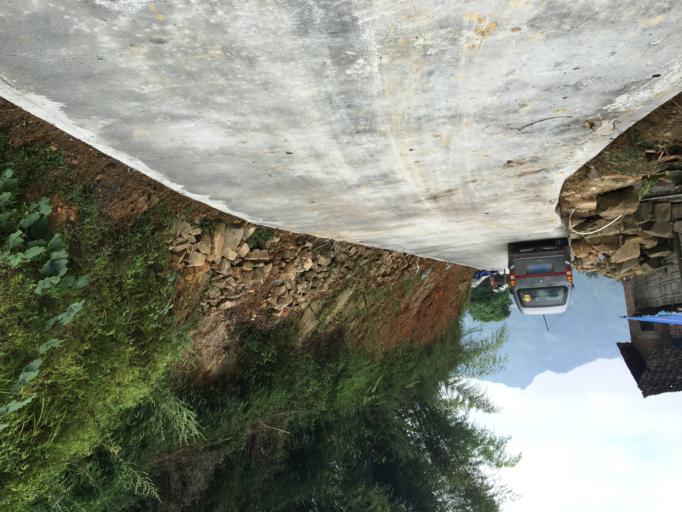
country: CN
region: Guangxi Zhuangzu Zizhiqu
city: Tongle
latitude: 25.2972
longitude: 106.1636
